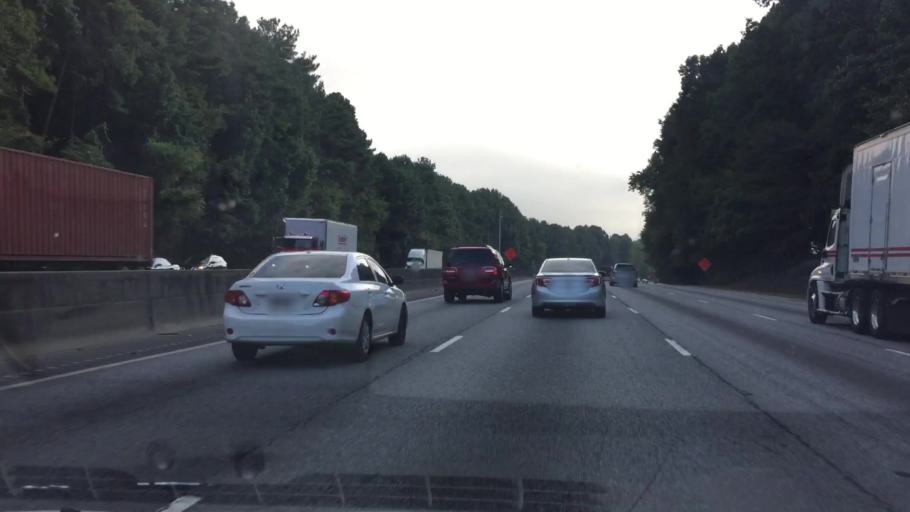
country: US
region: Georgia
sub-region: DeKalb County
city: Gresham Park
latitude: 33.6873
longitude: -84.3061
